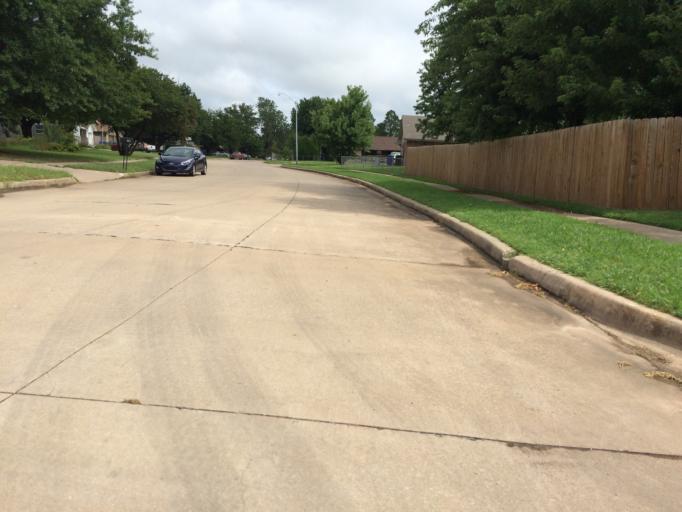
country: US
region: Oklahoma
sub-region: Cleveland County
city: Hall Park
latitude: 35.2227
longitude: -97.4181
